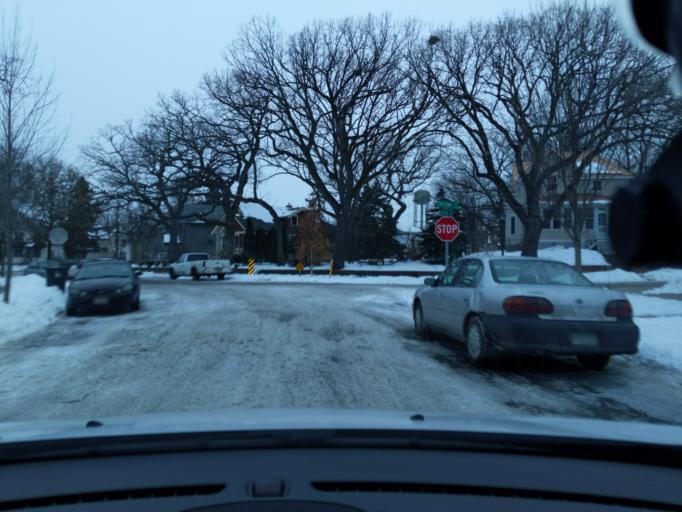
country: US
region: Minnesota
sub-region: Ramsey County
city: Falcon Heights
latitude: 44.9644
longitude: -93.1794
